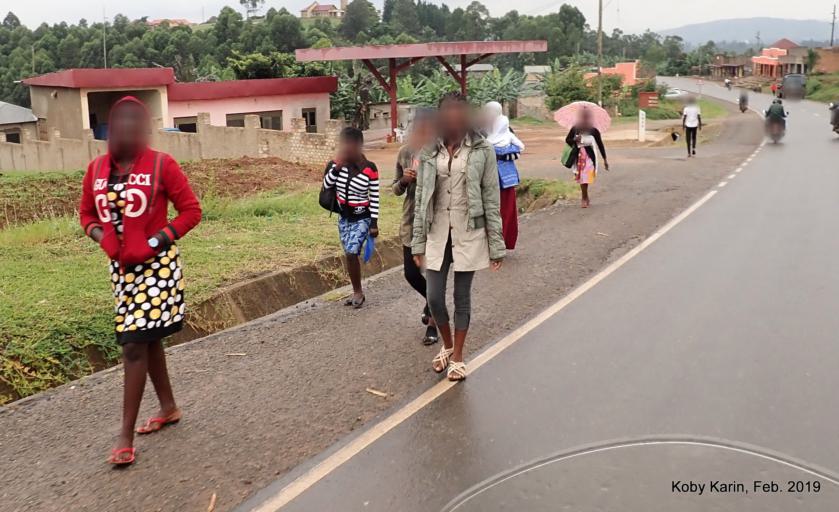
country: UG
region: Western Region
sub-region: Bushenyi District
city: Bushenyi
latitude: -0.5537
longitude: 30.1363
